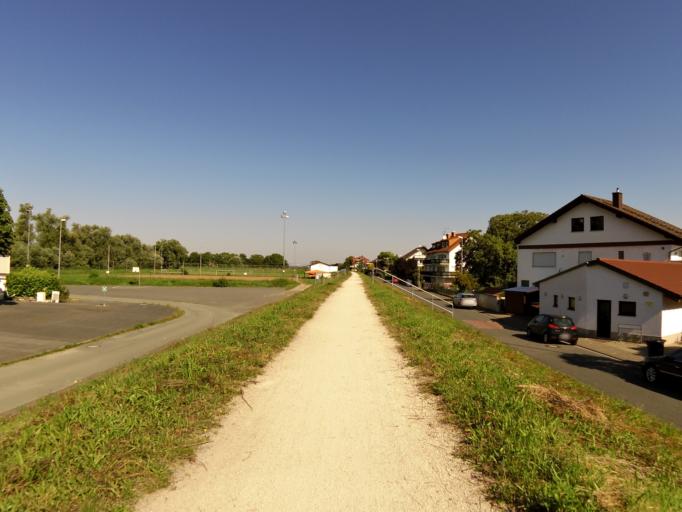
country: DE
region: Hesse
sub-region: Regierungsbezirk Darmstadt
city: Stockstadt am Rhein
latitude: 49.8361
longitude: 8.4628
